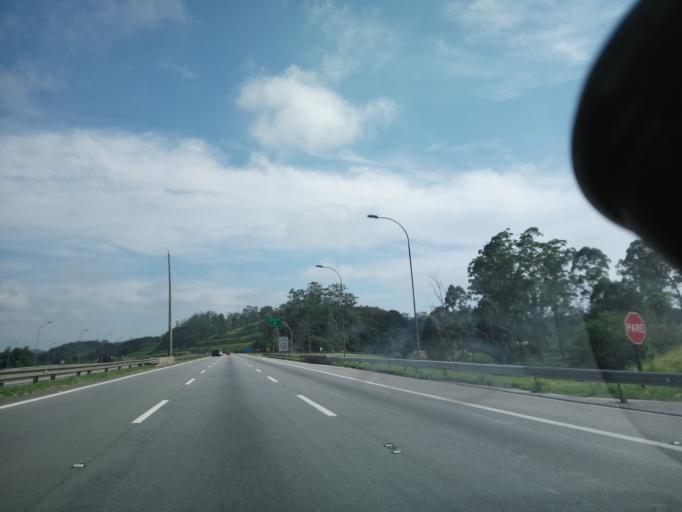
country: BR
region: Sao Paulo
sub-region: Itapecerica Da Serra
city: Itapecerica da Serra
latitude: -23.6900
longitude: -46.8187
